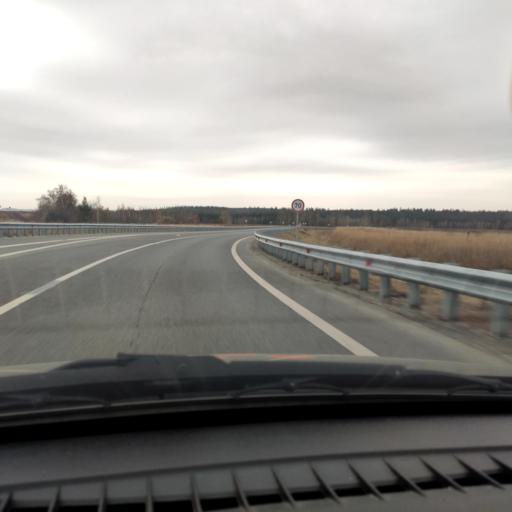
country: RU
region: Samara
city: Bereza
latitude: 53.4926
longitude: 50.1173
